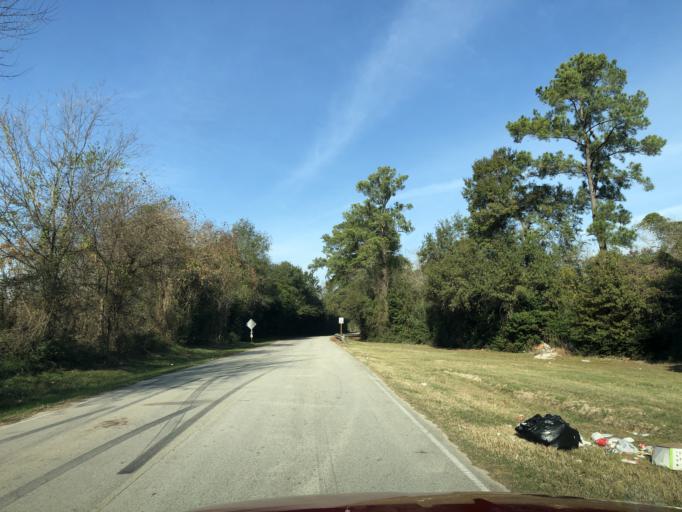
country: US
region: Texas
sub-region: Harris County
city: Tomball
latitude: 30.0425
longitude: -95.5459
